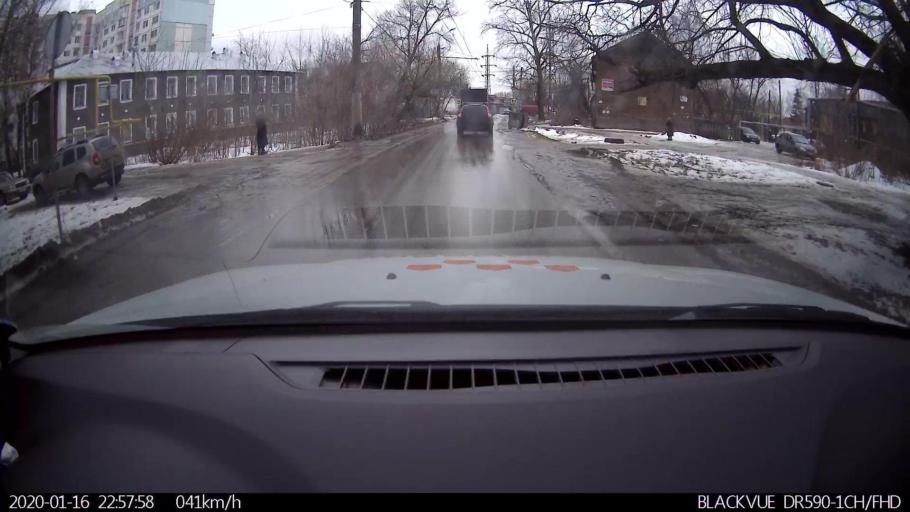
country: RU
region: Nizjnij Novgorod
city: Nizhniy Novgorod
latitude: 56.2899
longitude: 43.9086
